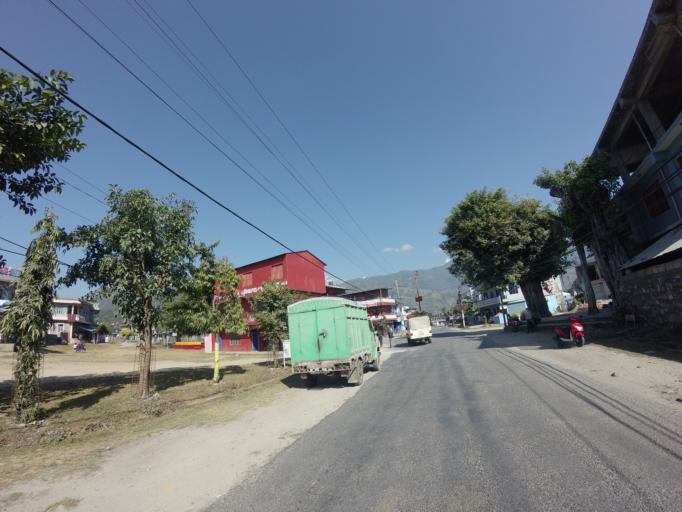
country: NP
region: Western Region
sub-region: Gandaki Zone
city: Pokhara
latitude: 28.2629
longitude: 83.9795
